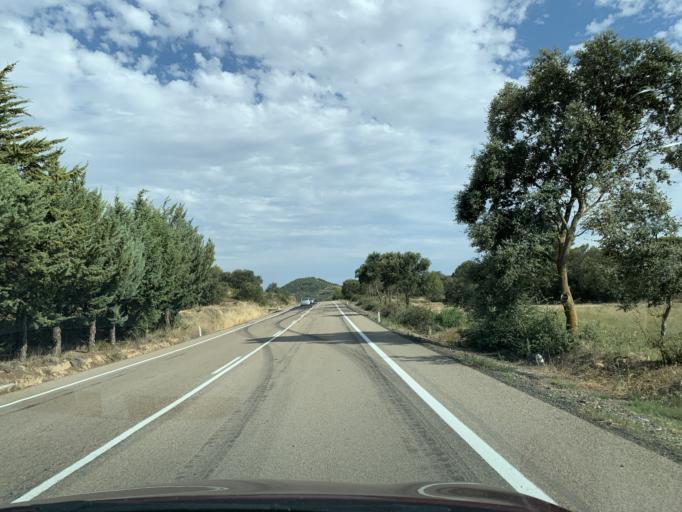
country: ES
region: Aragon
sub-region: Provincia de Huesca
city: Ayerbe
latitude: 42.2882
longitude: -0.7136
